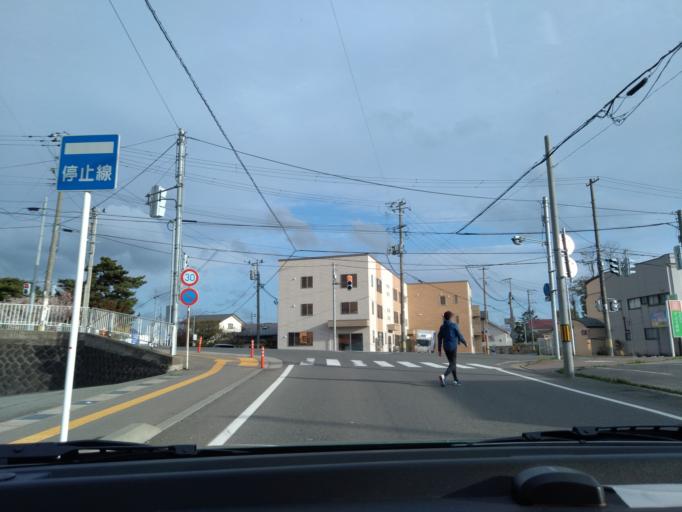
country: JP
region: Akita
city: Akita Shi
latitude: 39.7557
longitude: 140.0747
